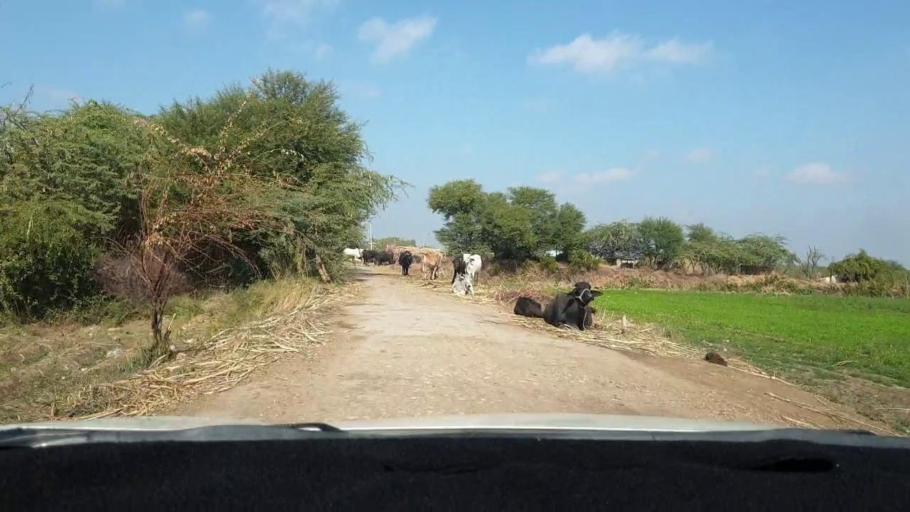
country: PK
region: Sindh
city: Berani
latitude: 25.7280
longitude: 68.9740
